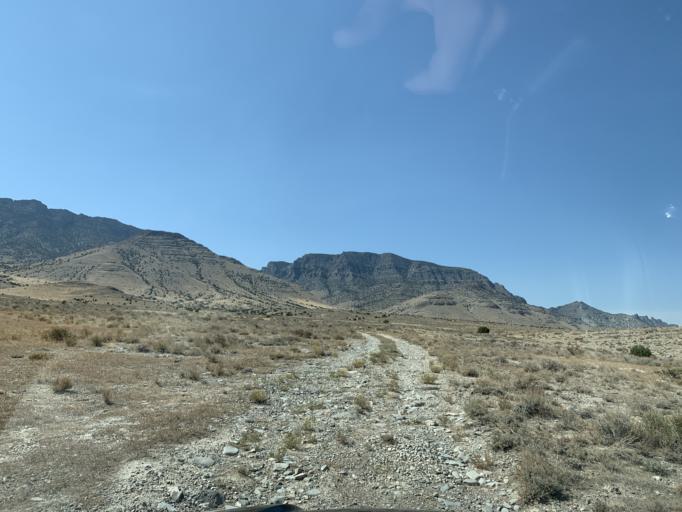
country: US
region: Utah
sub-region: Beaver County
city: Milford
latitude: 38.9760
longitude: -113.4575
